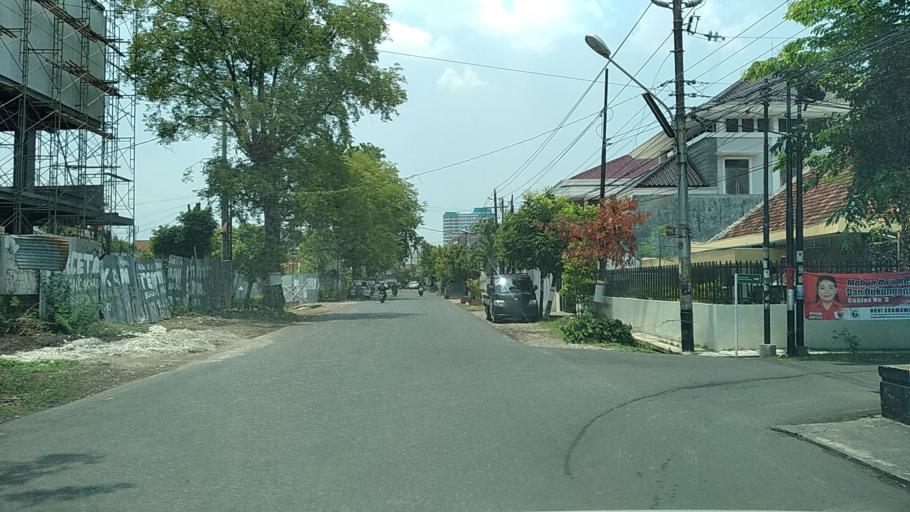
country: ID
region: Central Java
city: Semarang
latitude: -6.9941
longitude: 110.4360
